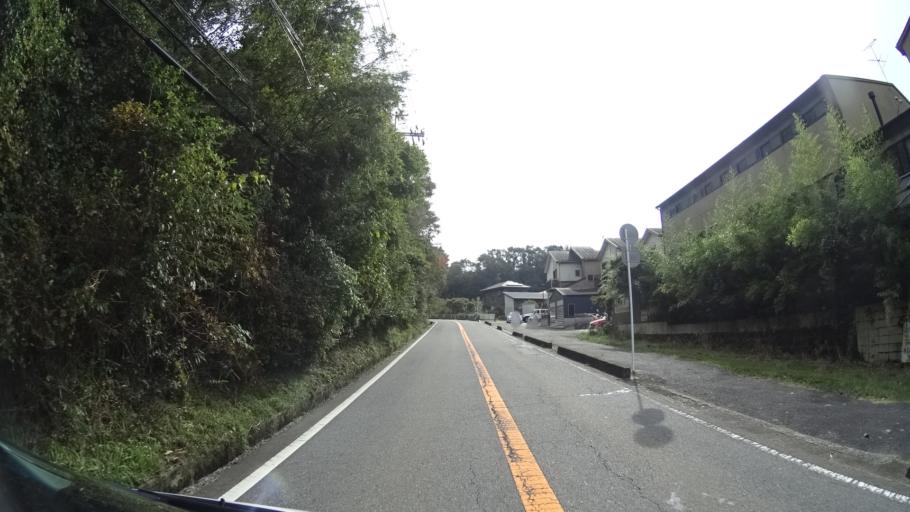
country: JP
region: Shiga Prefecture
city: Otsu-shi
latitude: 35.0345
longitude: 135.8307
